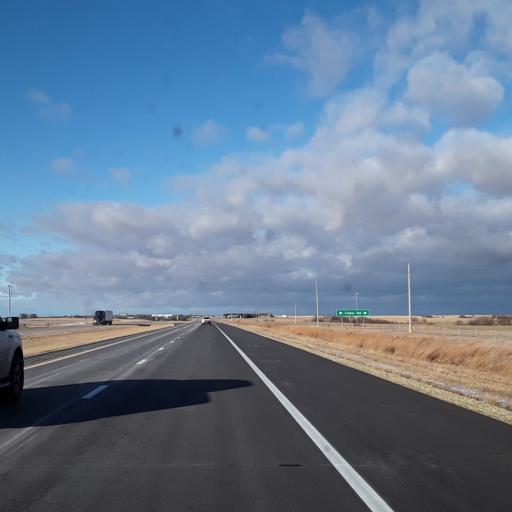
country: US
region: Kansas
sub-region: Republic County
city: Belleville
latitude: 39.9691
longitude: -97.6131
